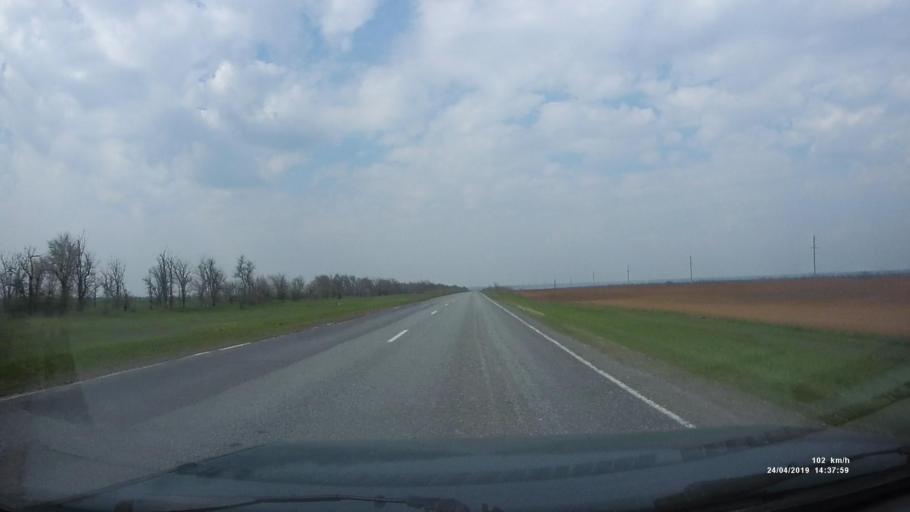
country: RU
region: Rostov
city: Remontnoye
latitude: 46.3943
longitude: 43.8863
